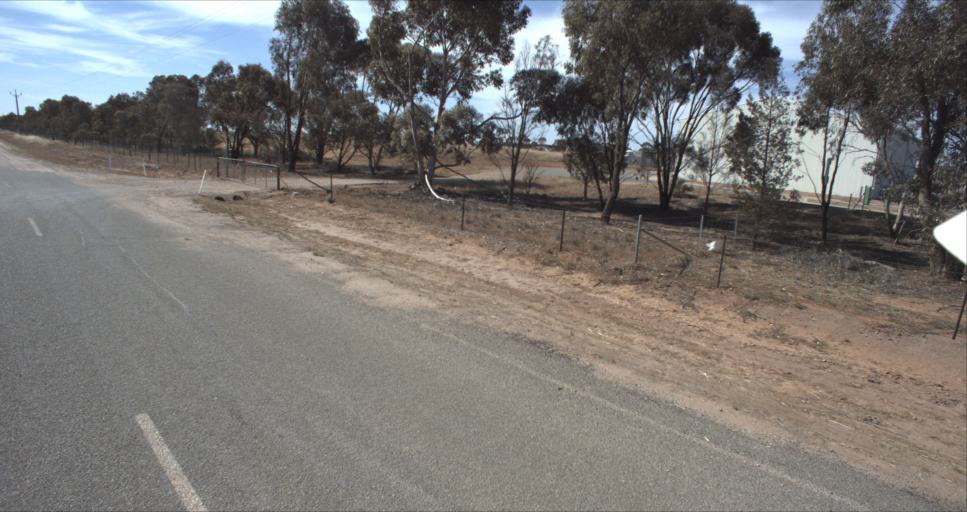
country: AU
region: New South Wales
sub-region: Leeton
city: Leeton
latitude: -34.5645
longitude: 146.4876
